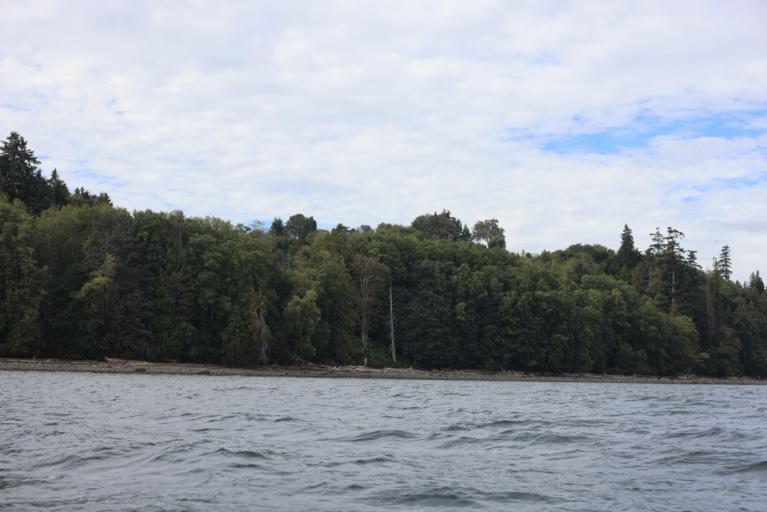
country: CA
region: British Columbia
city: Nanaimo
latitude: 49.2512
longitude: -124.0346
